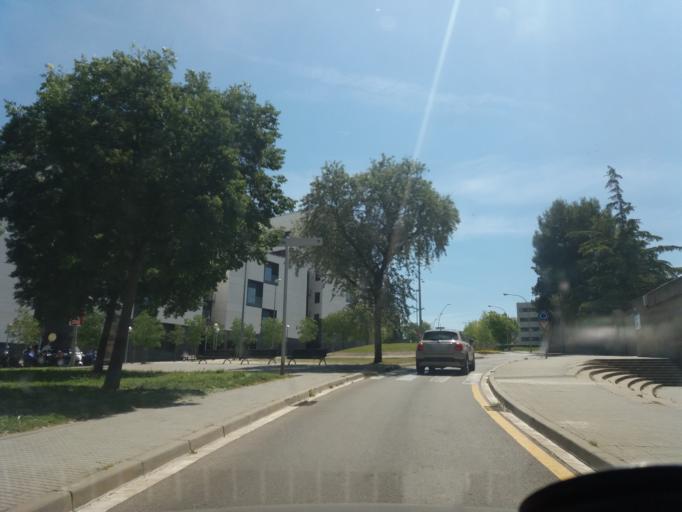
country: ES
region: Catalonia
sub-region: Provincia de Barcelona
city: Manresa
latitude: 41.7207
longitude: 1.8358
